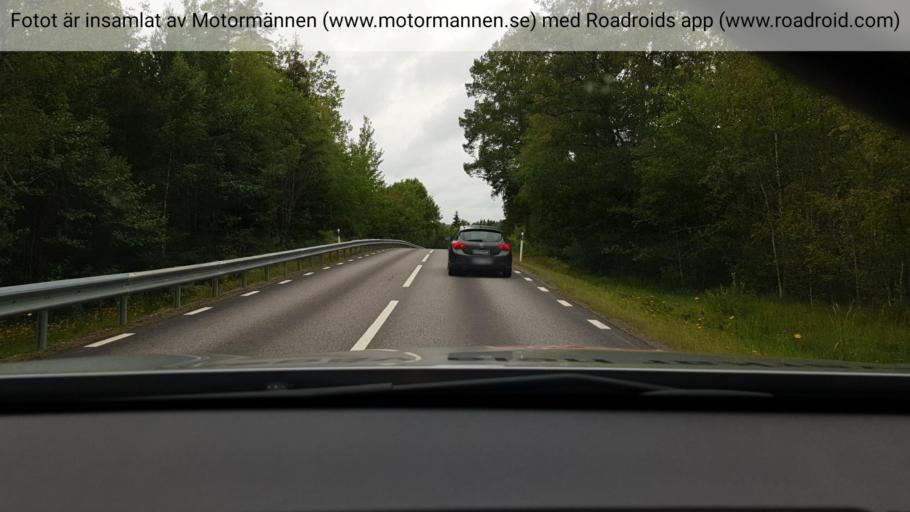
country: SE
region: Soedermanland
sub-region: Flens Kommun
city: Malmkoping
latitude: 59.0782
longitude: 16.8736
